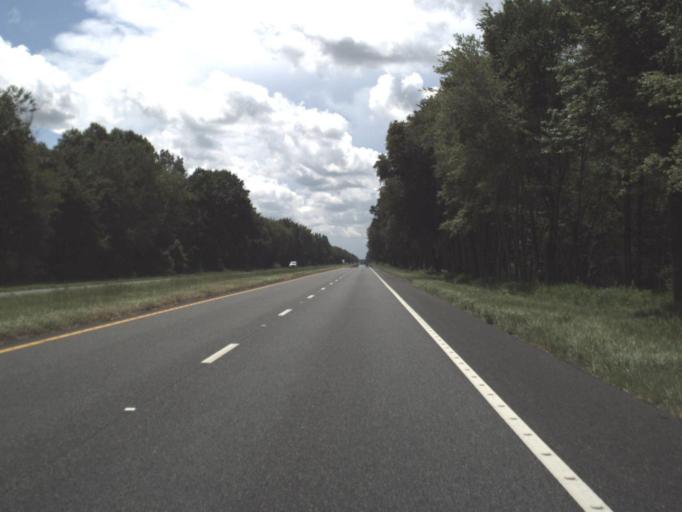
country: US
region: Florida
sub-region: Taylor County
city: Perry
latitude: 30.2253
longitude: -83.6776
